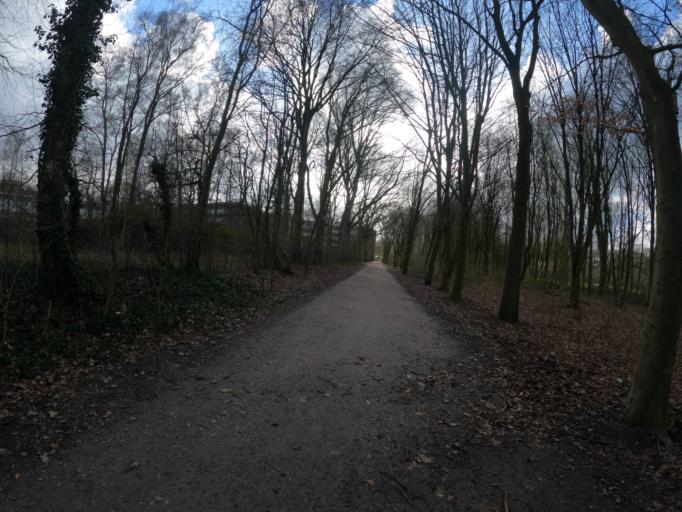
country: DE
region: Schleswig-Holstein
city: Bonningstedt
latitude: 53.6433
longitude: 9.9434
